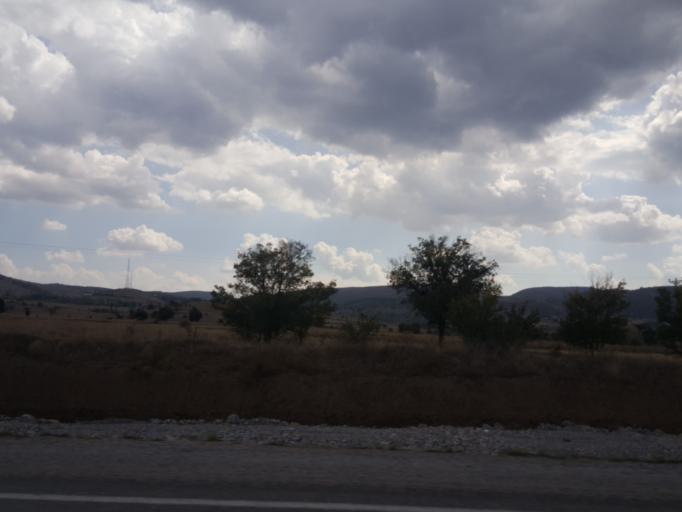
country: TR
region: Yozgat
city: Aydincik
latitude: 40.1780
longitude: 35.3817
